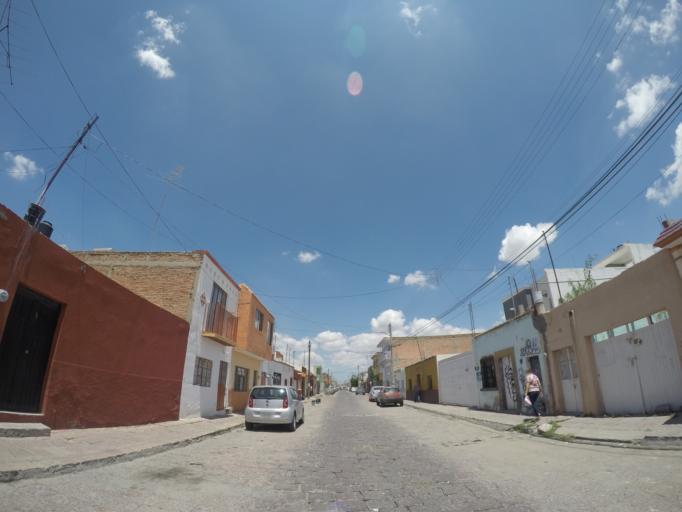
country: MX
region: San Luis Potosi
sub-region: San Luis Potosi
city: San Luis Potosi
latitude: 22.1519
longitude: -100.9607
